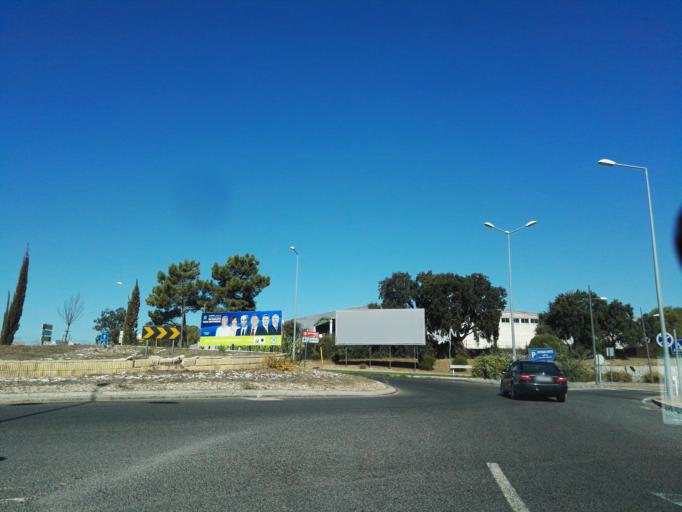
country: PT
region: Setubal
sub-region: Alcochete
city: Alcochete
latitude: 38.7515
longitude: -8.9433
